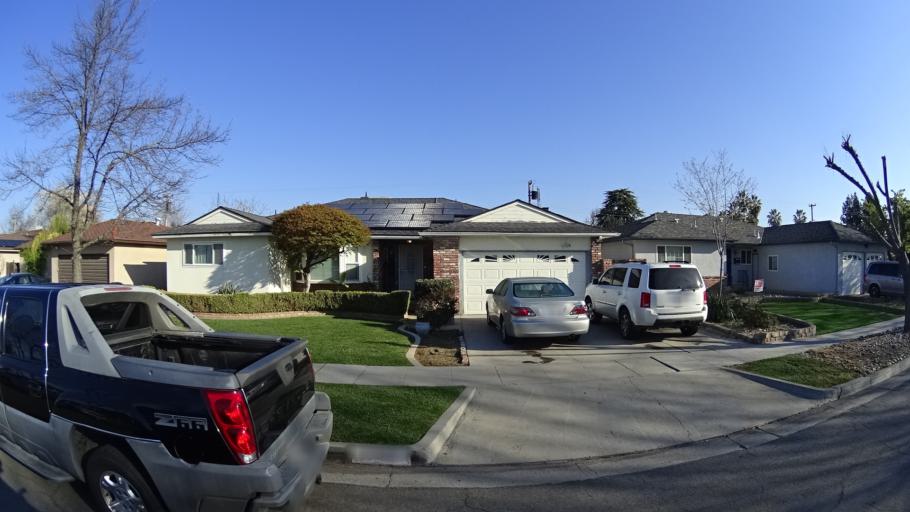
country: US
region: California
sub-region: Fresno County
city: Clovis
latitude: 36.8195
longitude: -119.7737
